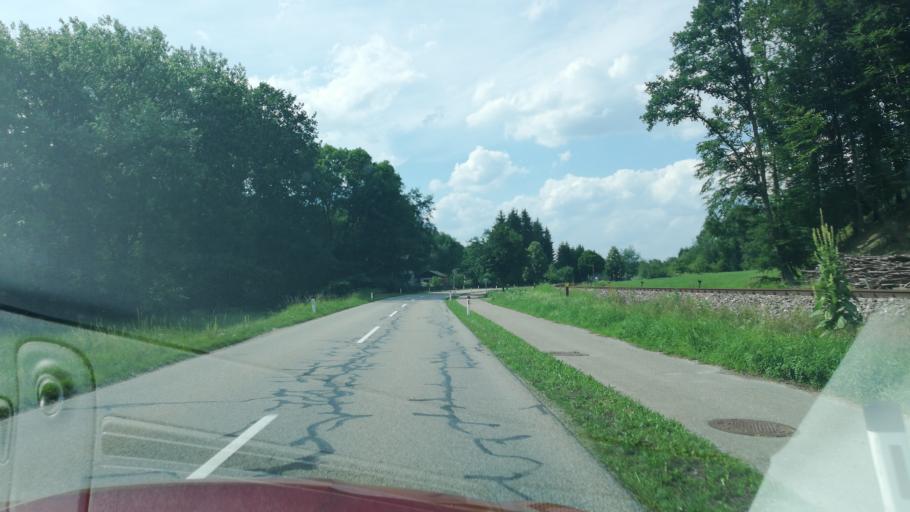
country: AT
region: Upper Austria
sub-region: Politischer Bezirk Vocklabruck
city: Puhret
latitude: 48.0255
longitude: 13.7066
